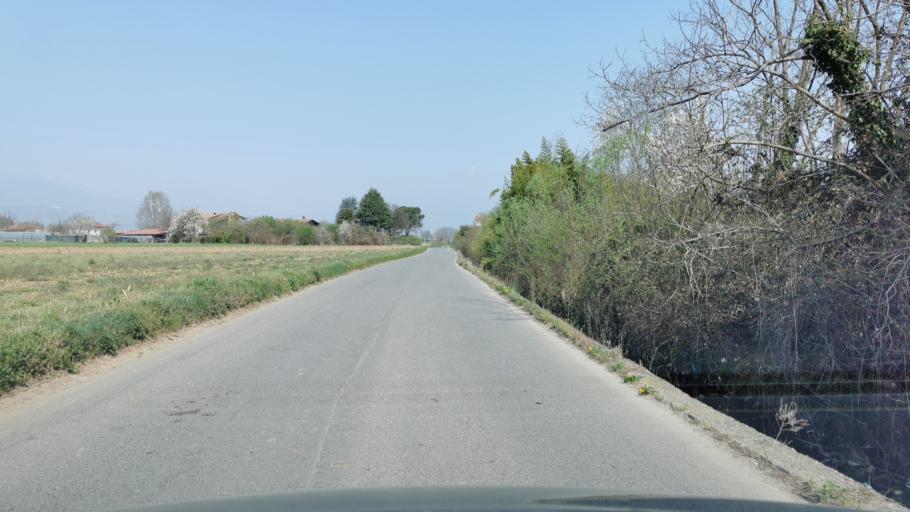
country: IT
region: Piedmont
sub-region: Provincia di Torino
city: Rivarolo Canavese
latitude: 45.3239
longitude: 7.7122
